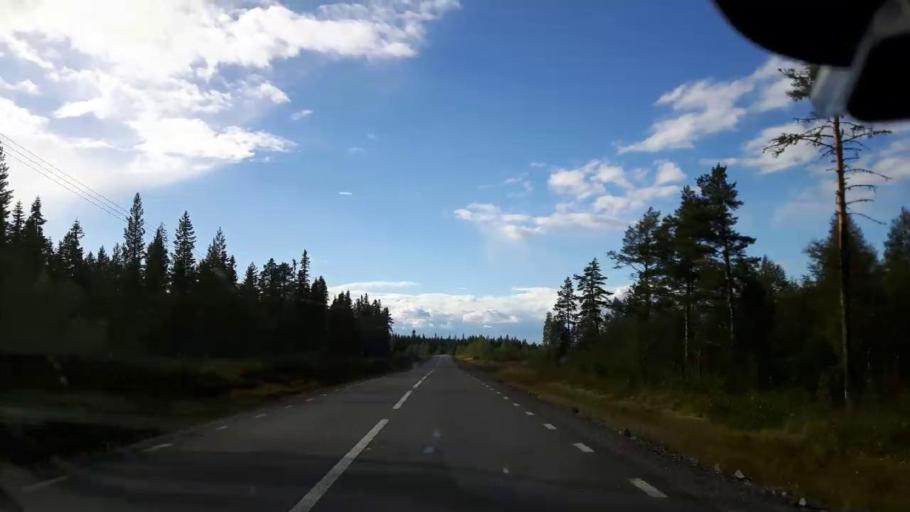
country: SE
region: Jaemtland
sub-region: Stroemsunds Kommun
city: Stroemsund
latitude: 63.5775
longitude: 15.7441
